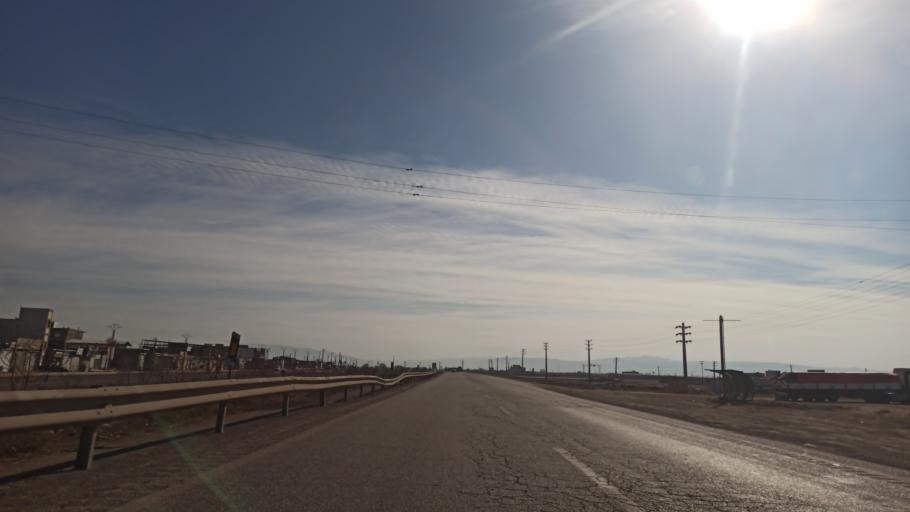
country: IR
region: Qazvin
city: Bu'in Zahra
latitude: 35.8476
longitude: 50.0605
